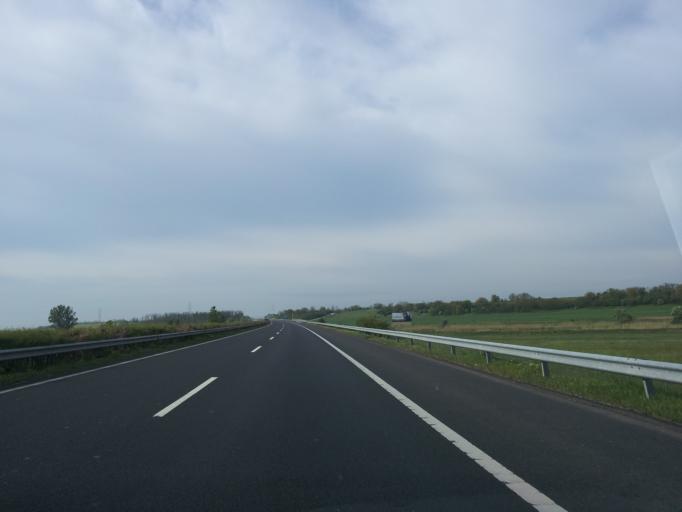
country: HU
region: Fejer
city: Rackeresztur
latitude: 47.2238
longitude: 18.8198
